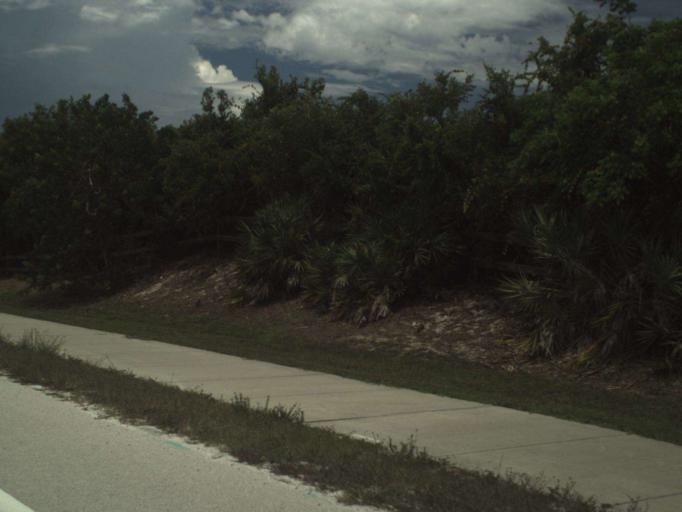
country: US
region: Florida
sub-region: Saint Lucie County
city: Indian River Estates
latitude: 27.3651
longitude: -80.2495
